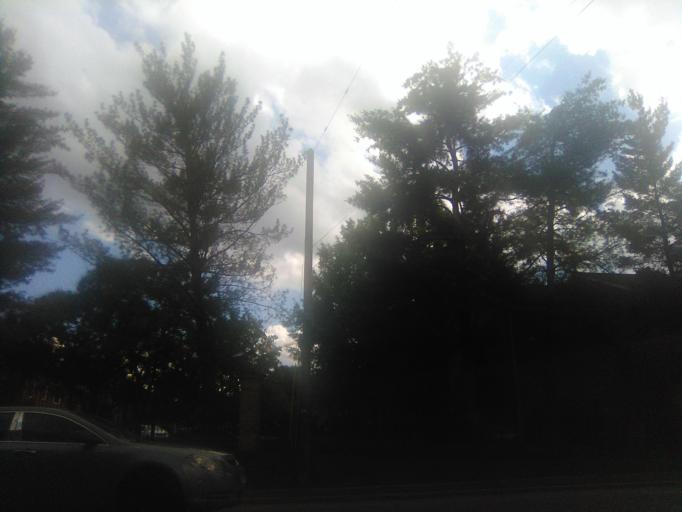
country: US
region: Tennessee
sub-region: Davidson County
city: Belle Meade
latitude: 36.1088
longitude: -86.8286
